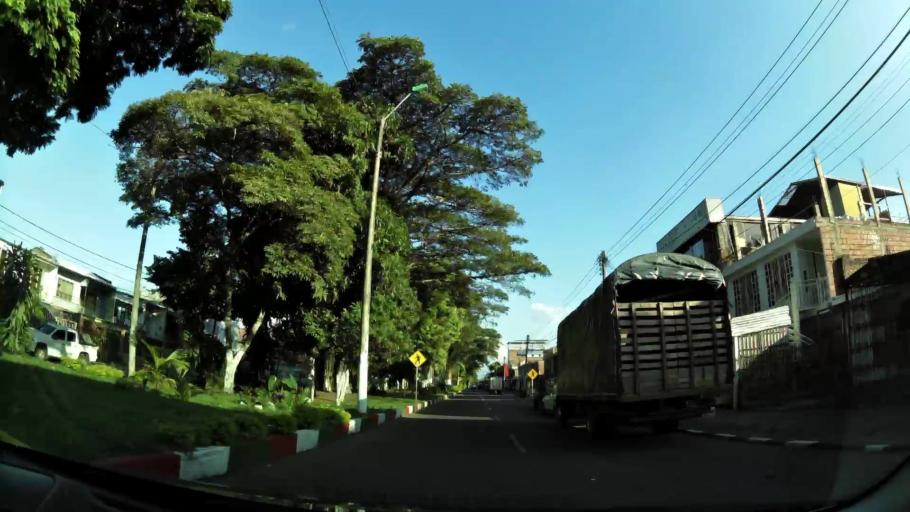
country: CO
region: Valle del Cauca
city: Cali
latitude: 3.4147
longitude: -76.5104
